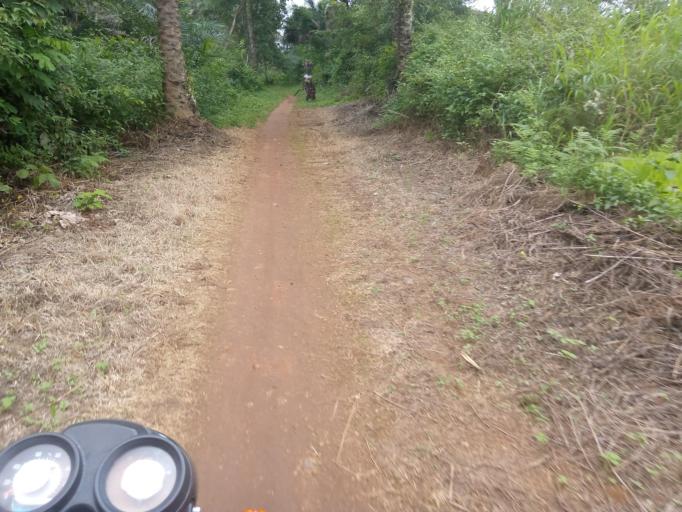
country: SL
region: Eastern Province
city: Buedu
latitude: 8.4807
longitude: -10.3292
